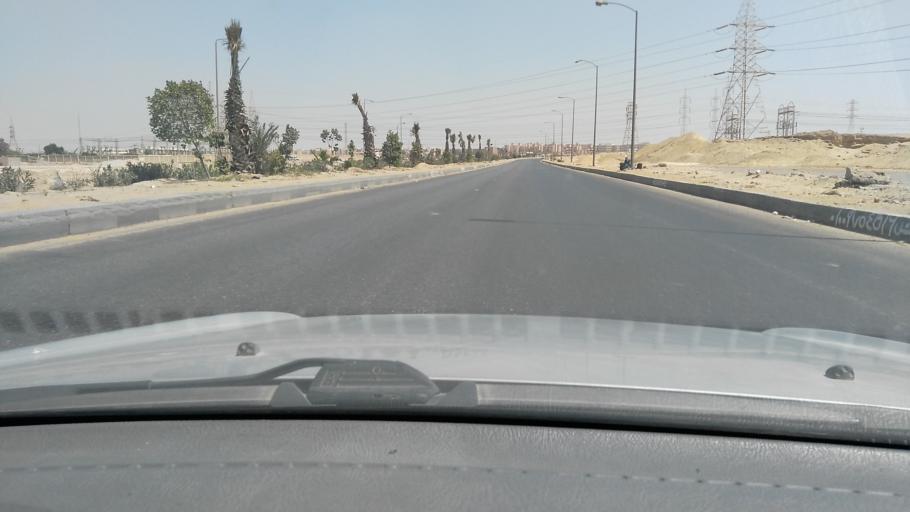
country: EG
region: Al Jizah
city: Madinat Sittah Uktubar
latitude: 29.9425
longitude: 30.9483
